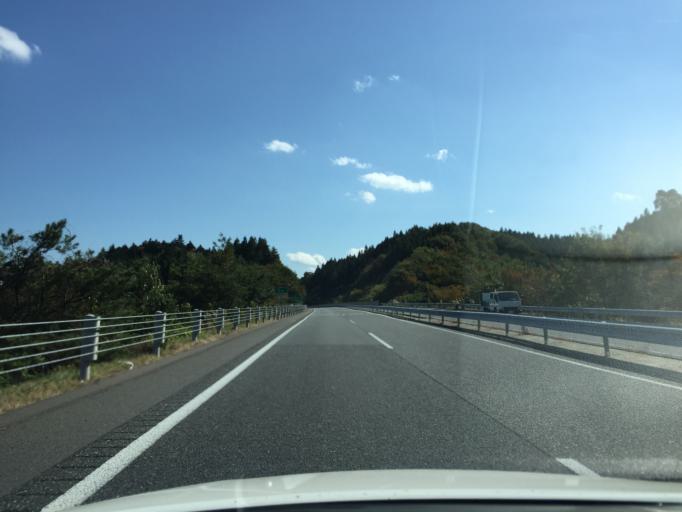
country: JP
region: Fukushima
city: Funehikimachi-funehiki
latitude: 37.2501
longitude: 140.6601
